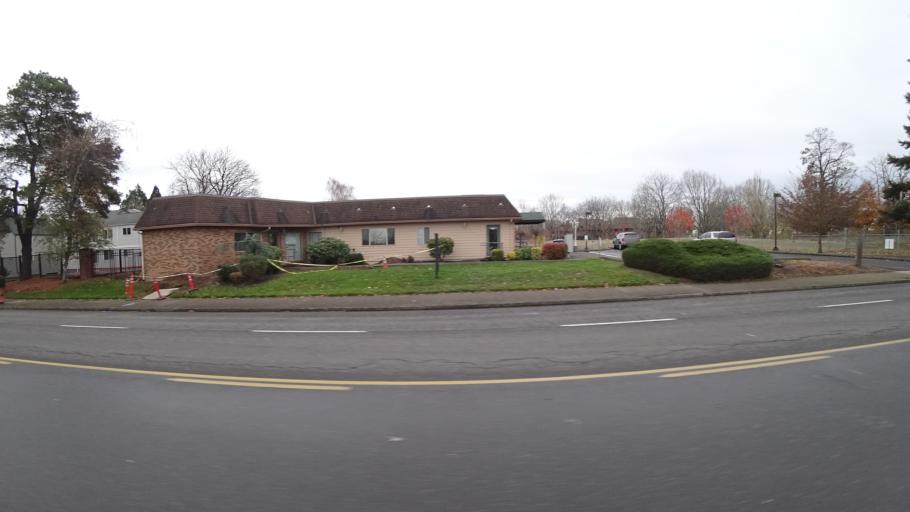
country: US
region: Oregon
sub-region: Multnomah County
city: Lents
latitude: 45.5158
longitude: -122.5560
